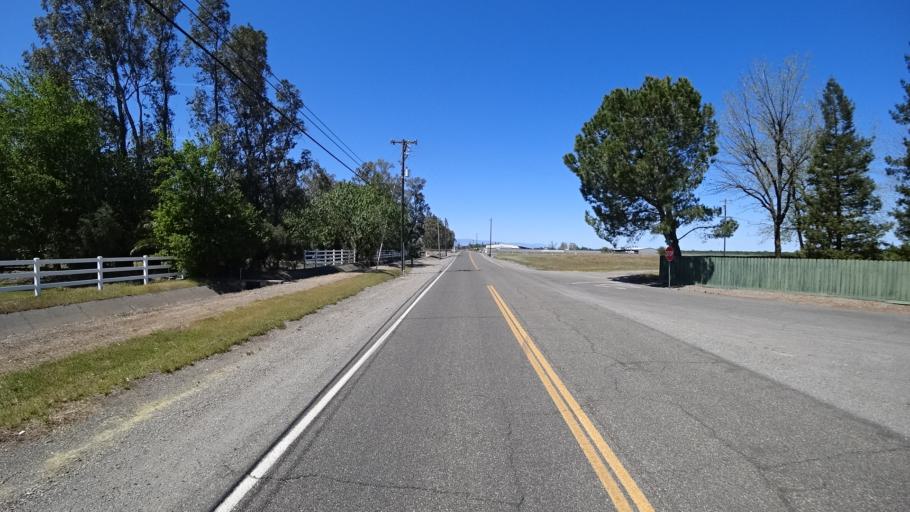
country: US
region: California
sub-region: Glenn County
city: Orland
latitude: 39.7324
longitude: -122.1592
